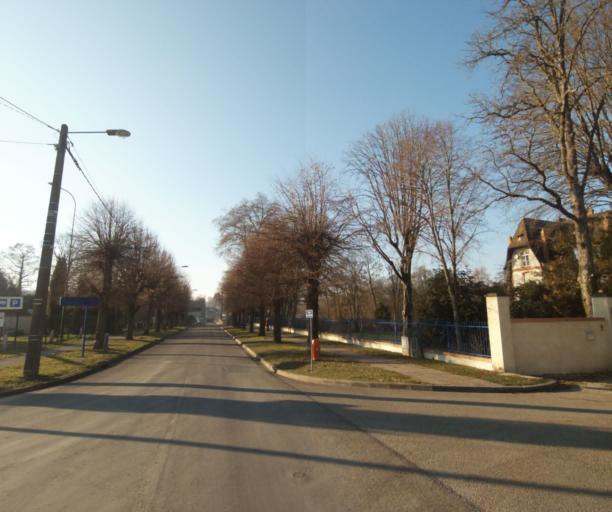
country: FR
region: Champagne-Ardenne
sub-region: Departement de la Haute-Marne
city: Bienville
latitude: 48.5836
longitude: 5.0444
